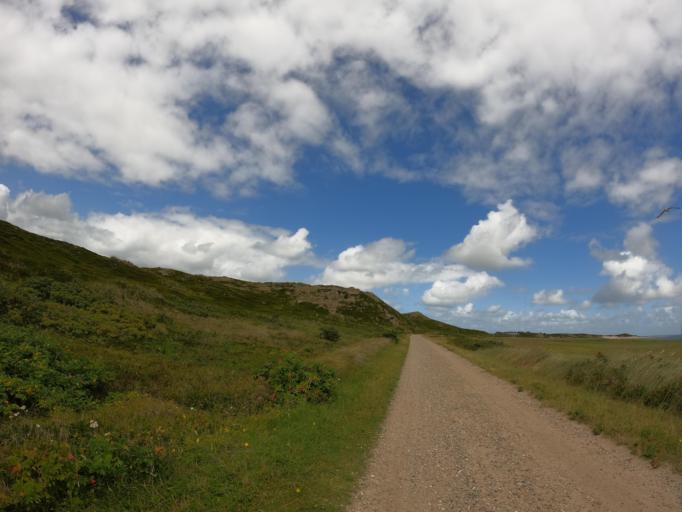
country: DE
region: Schleswig-Holstein
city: Tinnum
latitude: 54.7947
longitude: 8.2930
